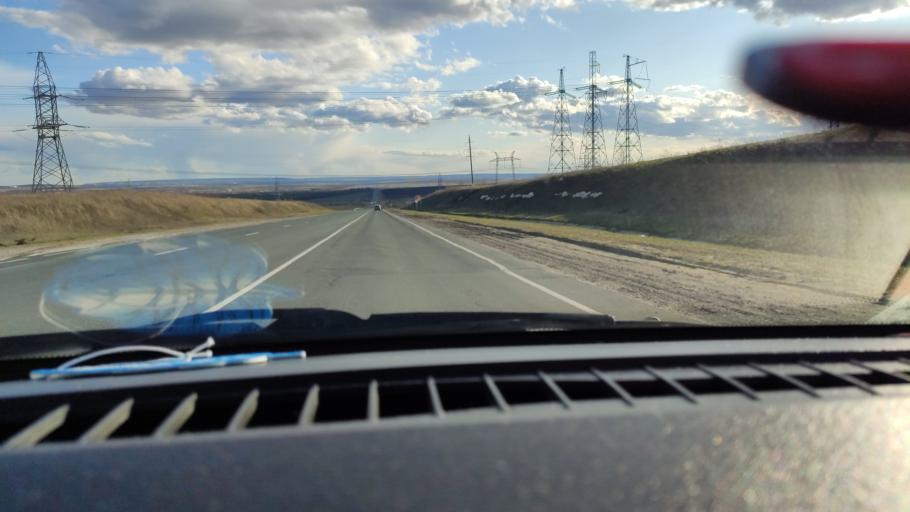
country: RU
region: Saratov
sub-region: Saratovskiy Rayon
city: Saratov
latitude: 51.7632
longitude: 46.0746
